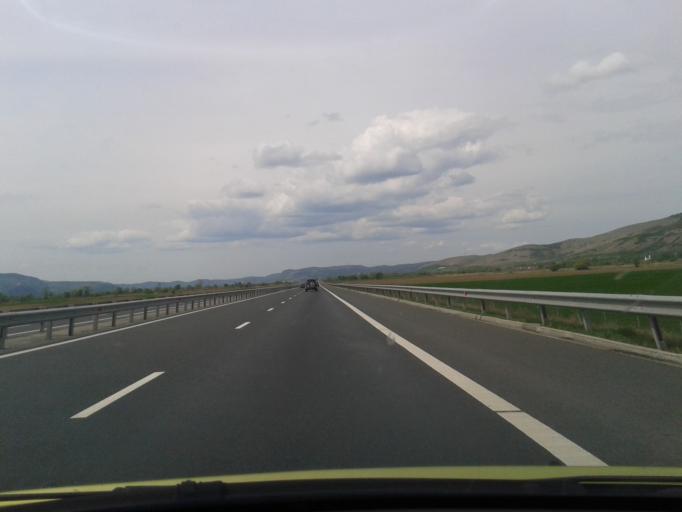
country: RO
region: Hunedoara
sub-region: Oras Simeria
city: Simeria
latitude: 45.8746
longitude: 23.0076
